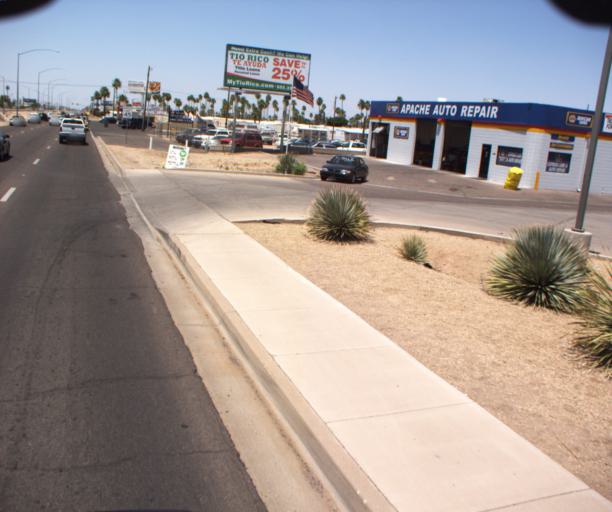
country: US
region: Arizona
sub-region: Pinal County
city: Apache Junction
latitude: 33.4154
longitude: -111.5985
